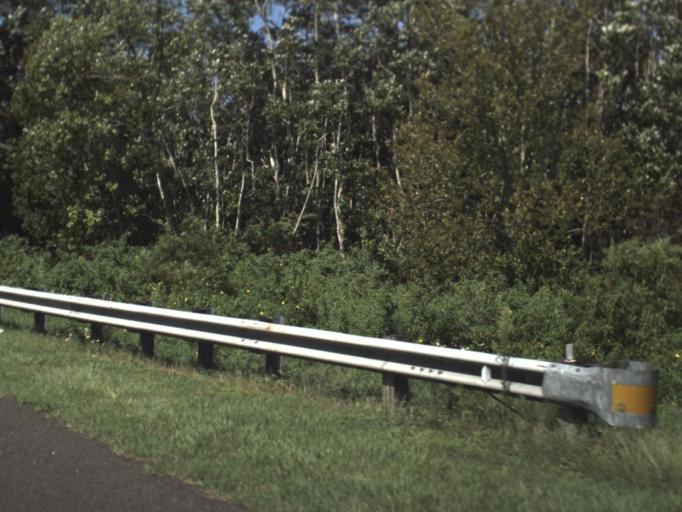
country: US
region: Florida
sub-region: Polk County
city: Lake Alfred
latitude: 28.1021
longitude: -81.7071
